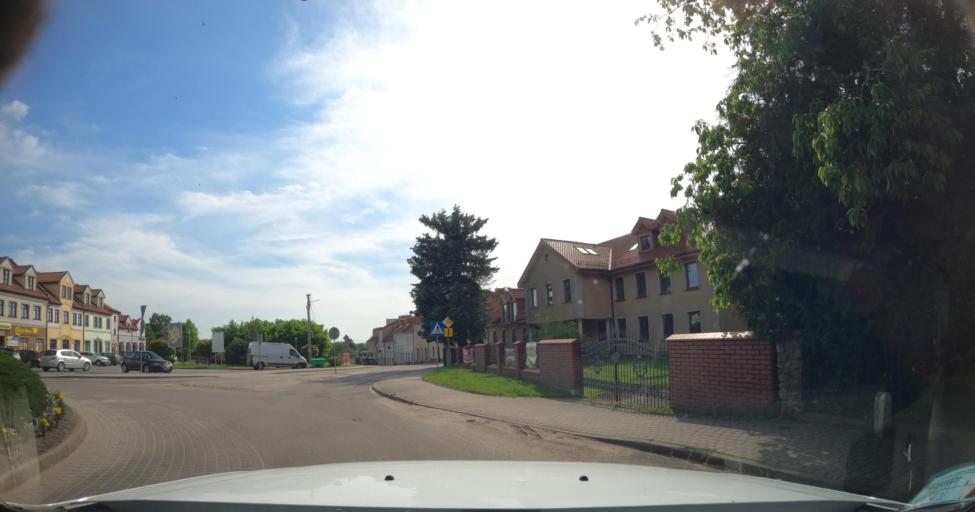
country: PL
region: Warmian-Masurian Voivodeship
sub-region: Powiat ostrodzki
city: Milakowo
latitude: 54.0103
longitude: 20.0721
